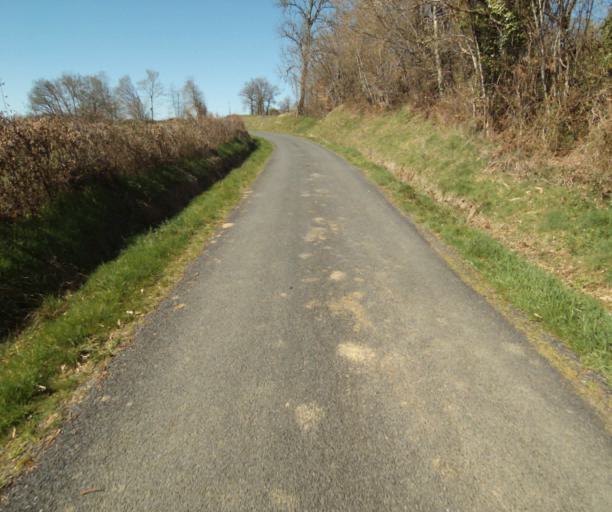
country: FR
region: Limousin
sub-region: Departement de la Correze
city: Chamboulive
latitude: 45.4432
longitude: 1.6984
